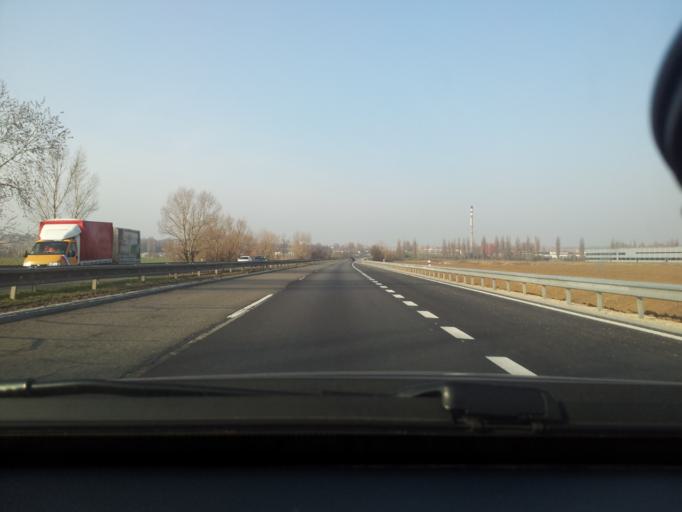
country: SK
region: Nitriansky
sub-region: Okres Nitra
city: Nitra
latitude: 48.3246
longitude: 18.0590
